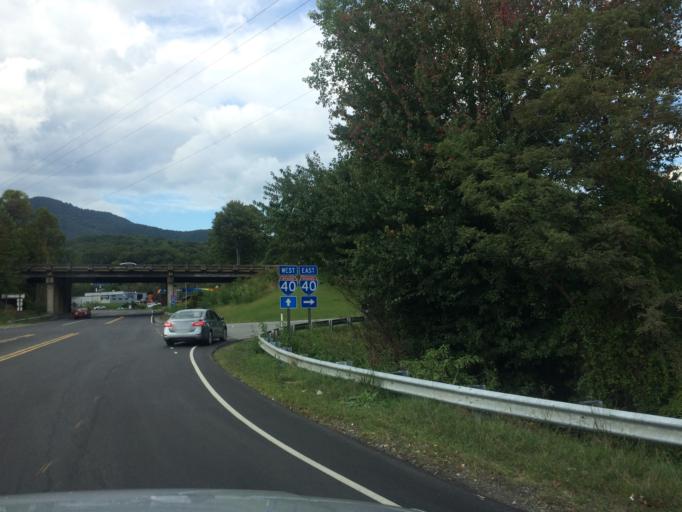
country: US
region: North Carolina
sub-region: Haywood County
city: Canton
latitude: 35.5412
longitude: -82.7525
